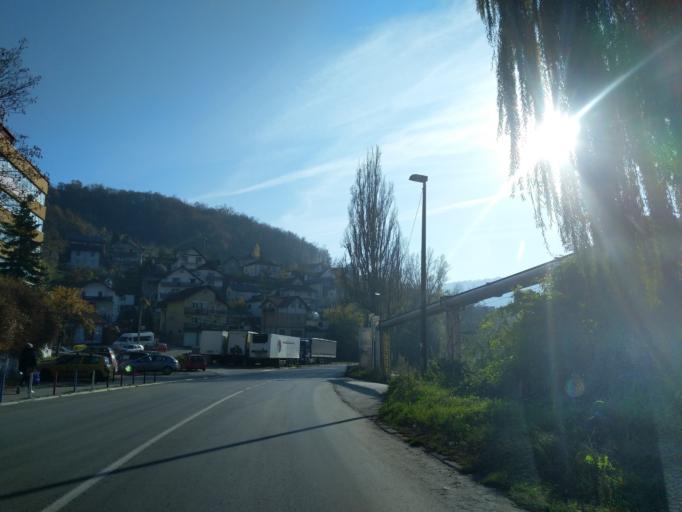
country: RS
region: Central Serbia
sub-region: Zlatiborski Okrug
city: Uzice
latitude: 43.8462
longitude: 19.8633
